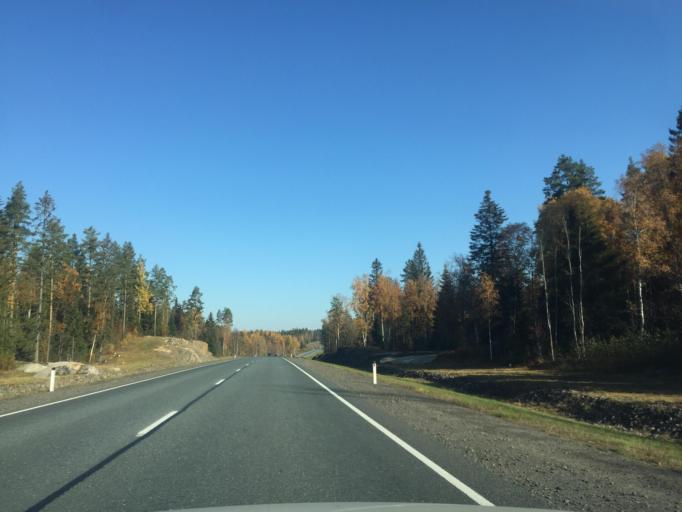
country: RU
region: Leningrad
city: Kuznechnoye
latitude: 61.3588
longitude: 29.8908
